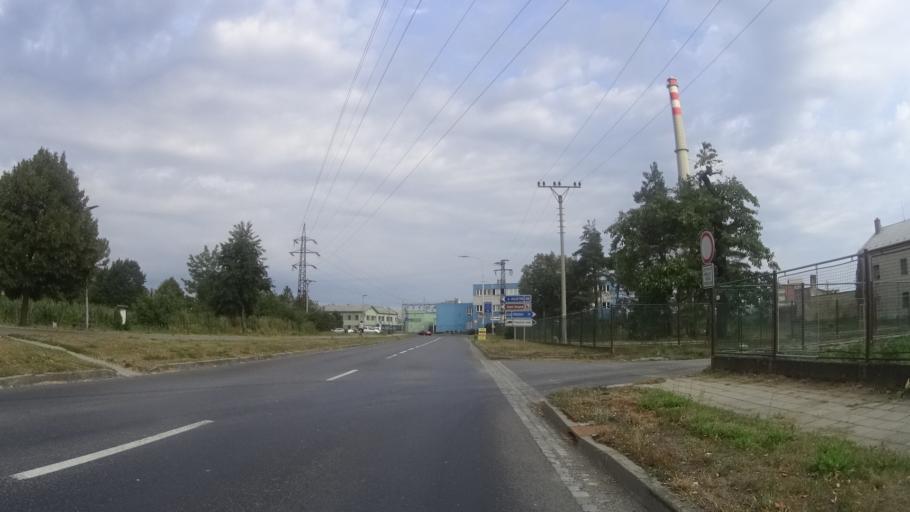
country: CZ
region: Zlin
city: Chropyne
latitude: 49.3567
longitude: 17.3722
